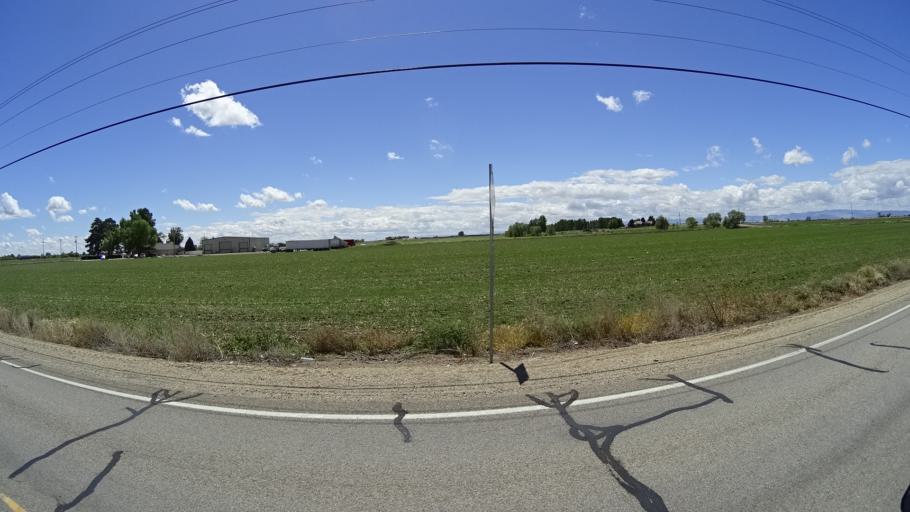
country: US
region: Idaho
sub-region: Ada County
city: Meridian
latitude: 43.5466
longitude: -116.3768
